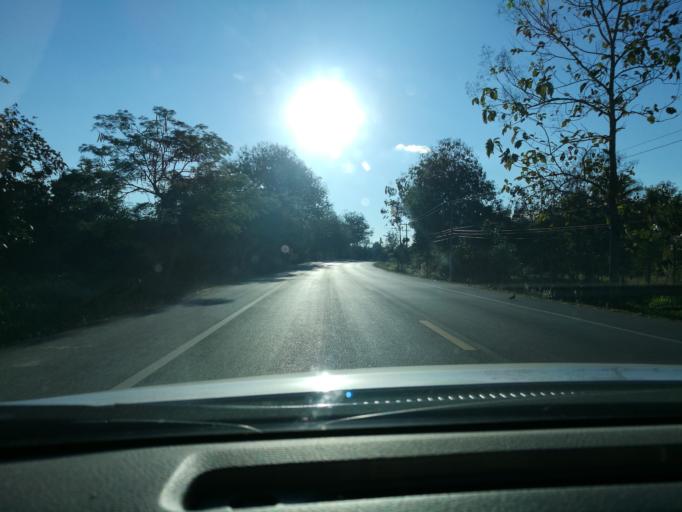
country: TH
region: Phitsanulok
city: Nakhon Thai
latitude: 17.0687
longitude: 100.8189
